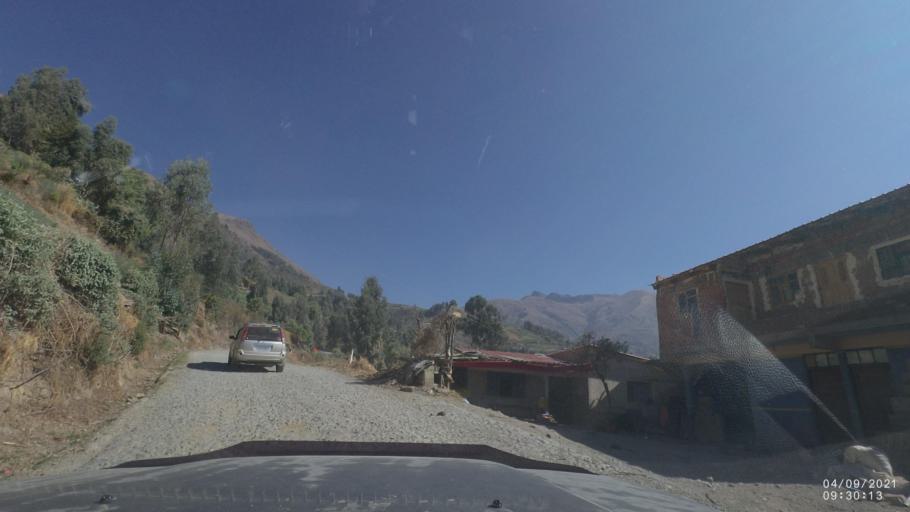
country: BO
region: Cochabamba
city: Sipe Sipe
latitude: -17.3540
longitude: -66.3754
